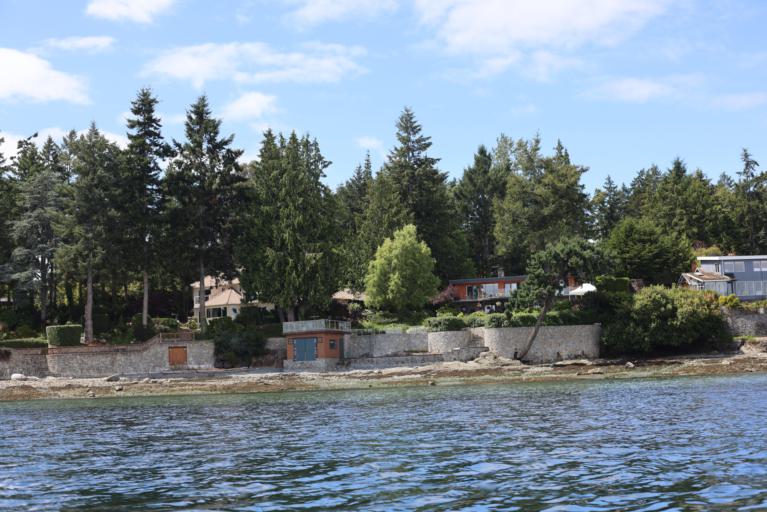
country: CA
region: British Columbia
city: North Saanich
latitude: 48.6103
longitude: -123.3952
